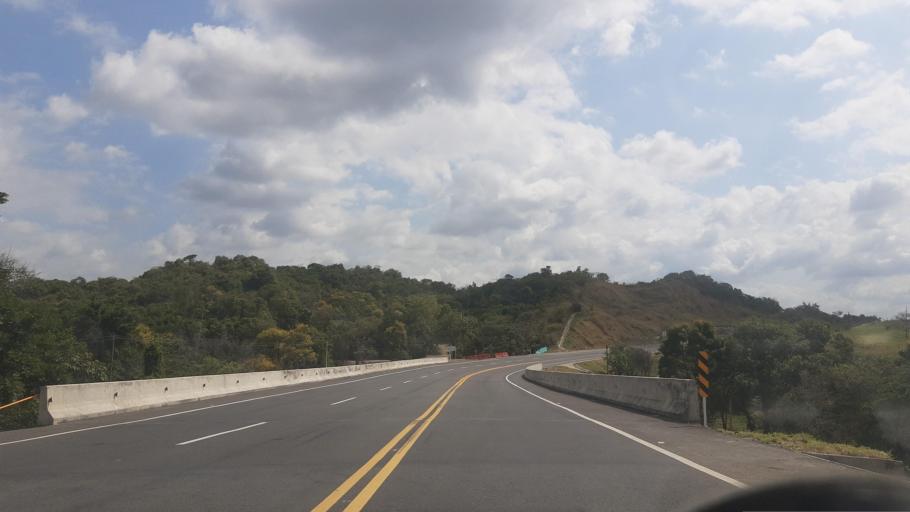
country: CO
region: Casanare
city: Monterrey
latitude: 4.8364
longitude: -72.8282
